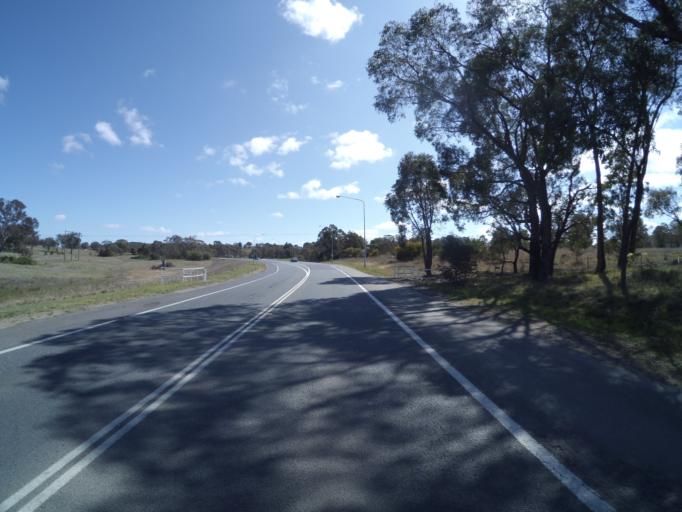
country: AU
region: New South Wales
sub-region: Queanbeyan
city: Queanbeyan
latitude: -35.3332
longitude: 149.2386
